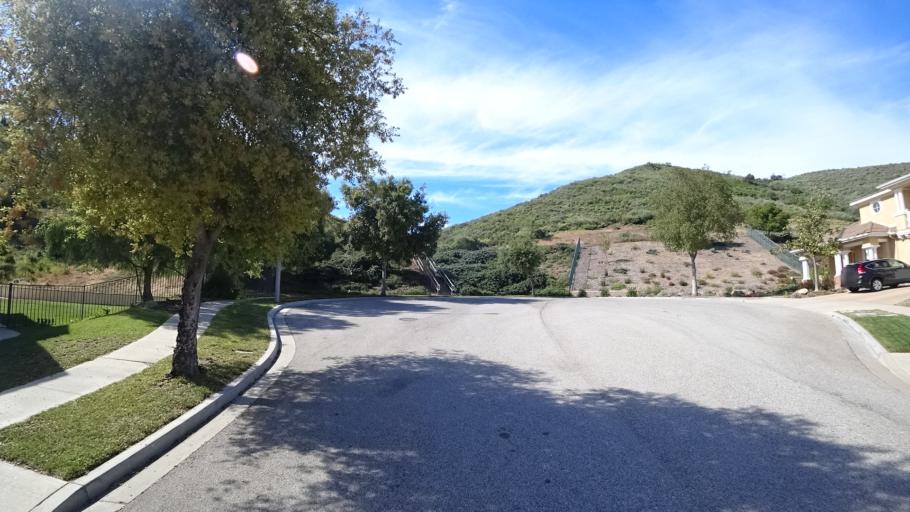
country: US
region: California
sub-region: Ventura County
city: Casa Conejo
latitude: 34.1697
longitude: -118.9787
